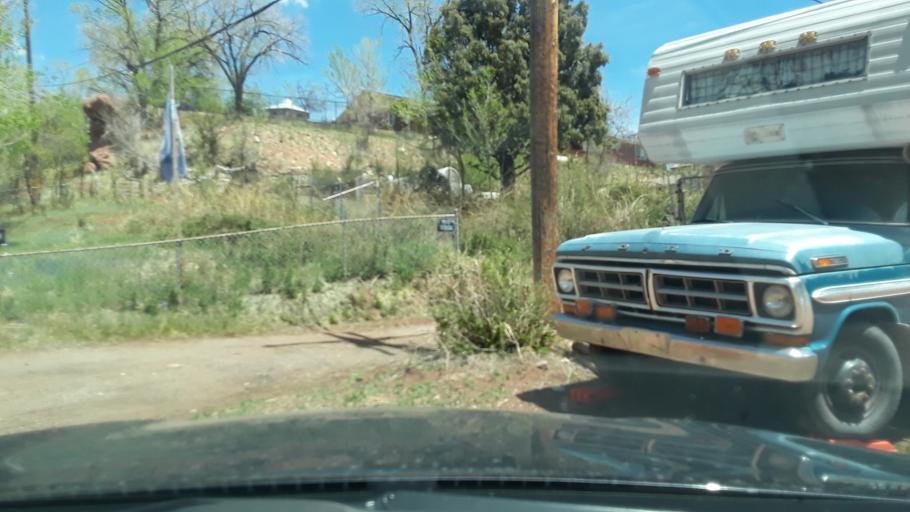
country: US
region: Colorado
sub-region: El Paso County
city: Manitou Springs
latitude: 38.8579
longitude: -104.8847
